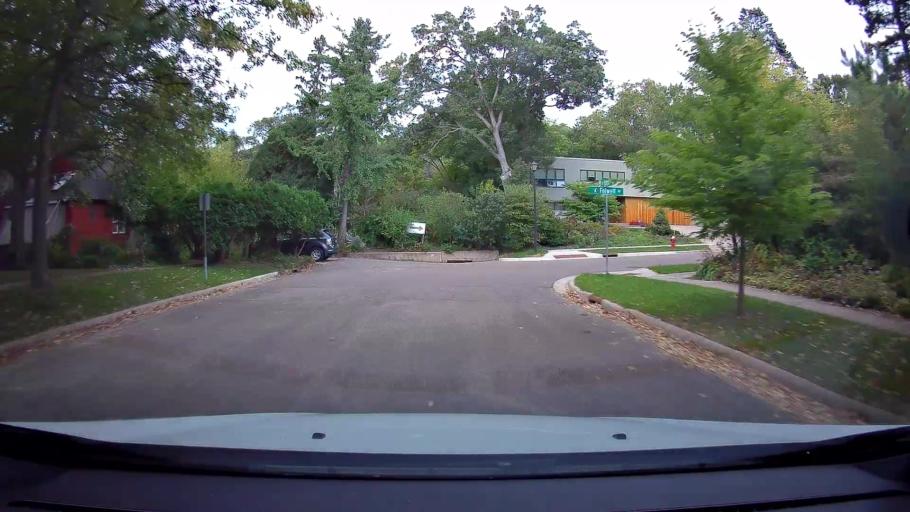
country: US
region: Minnesota
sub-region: Ramsey County
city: Lauderdale
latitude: 44.9890
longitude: -93.1971
